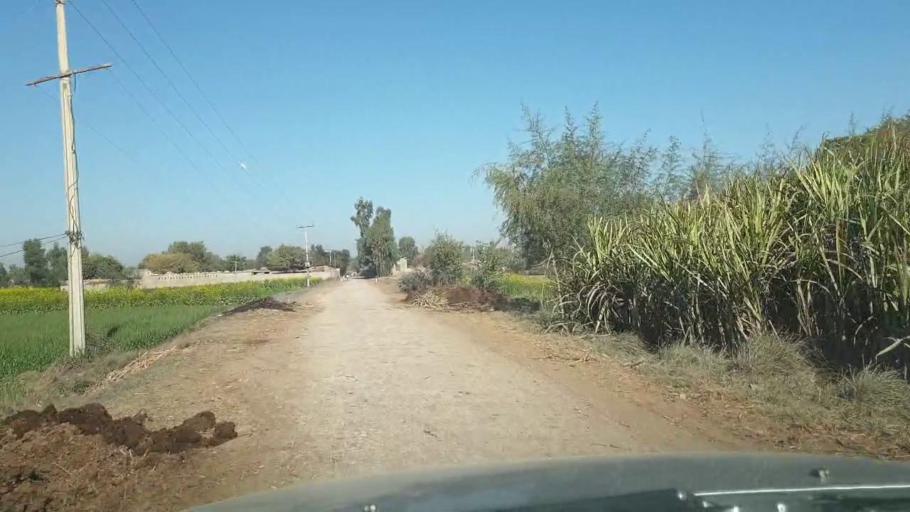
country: PK
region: Sindh
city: Ghotki
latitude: 28.0972
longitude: 69.3425
